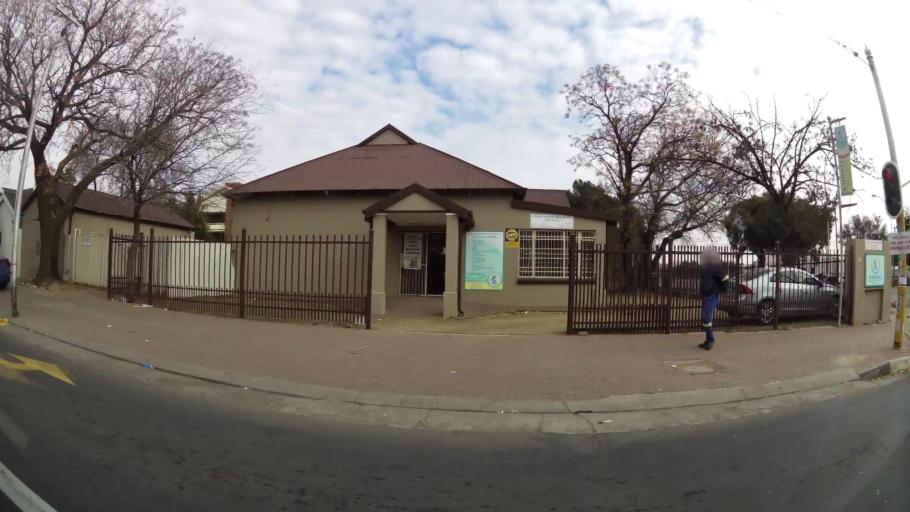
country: ZA
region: Orange Free State
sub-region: Mangaung Metropolitan Municipality
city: Bloemfontein
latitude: -29.1197
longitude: 26.2040
